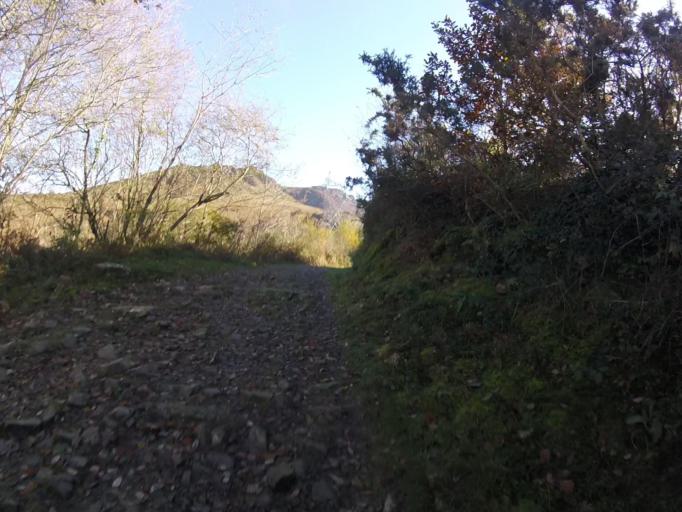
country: FR
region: Aquitaine
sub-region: Departement des Pyrenees-Atlantiques
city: Urrugne
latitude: 43.3318
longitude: -1.7352
